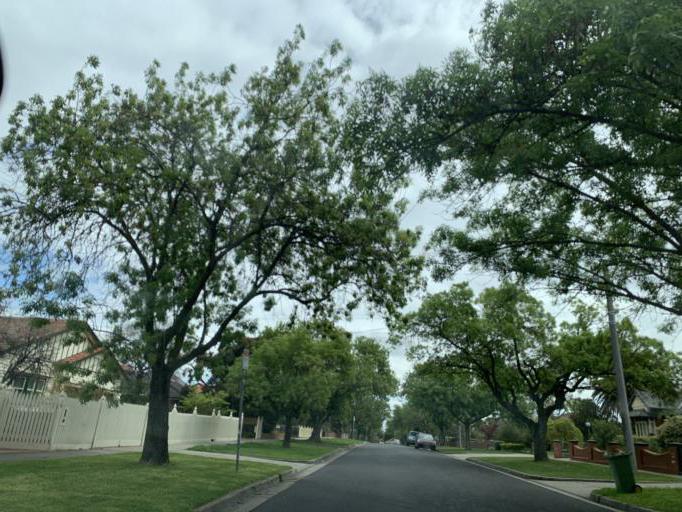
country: AU
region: Victoria
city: Thornbury
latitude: -37.7404
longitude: 144.9927
